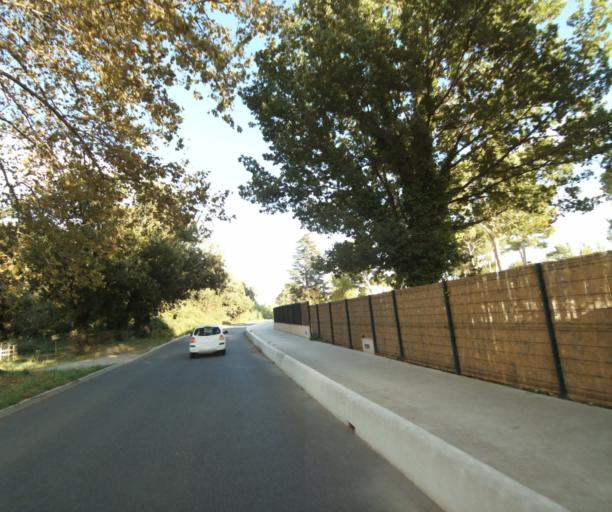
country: FR
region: Languedoc-Roussillon
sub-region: Departement des Pyrenees-Orientales
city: Argelers
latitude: 42.5735
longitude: 3.0193
